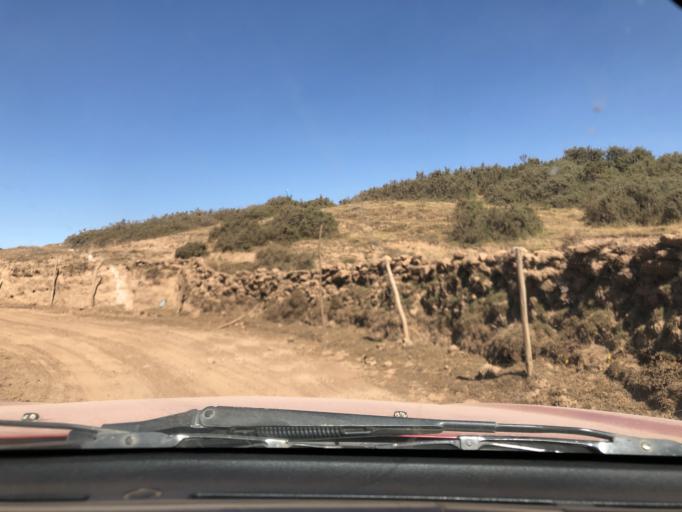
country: PE
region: Ayacucho
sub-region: Provincia de La Mar
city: Pampas
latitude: -13.1879
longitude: -73.8436
